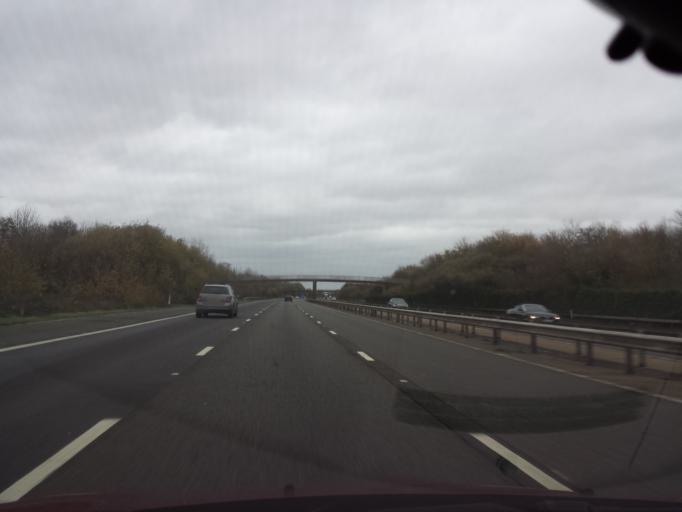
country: GB
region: England
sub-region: Surrey
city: Shepperton
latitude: 51.4020
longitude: -0.4495
